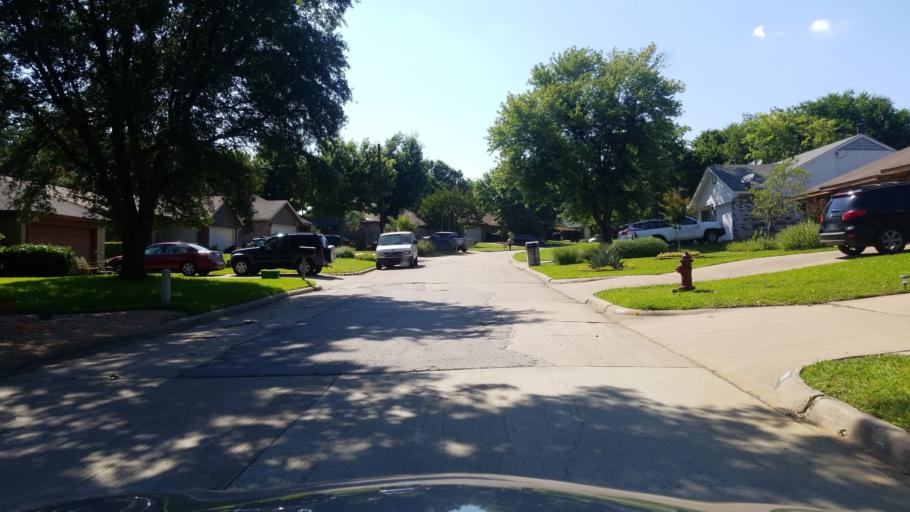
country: US
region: Texas
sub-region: Dallas County
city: Grand Prairie
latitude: 32.6787
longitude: -97.0167
